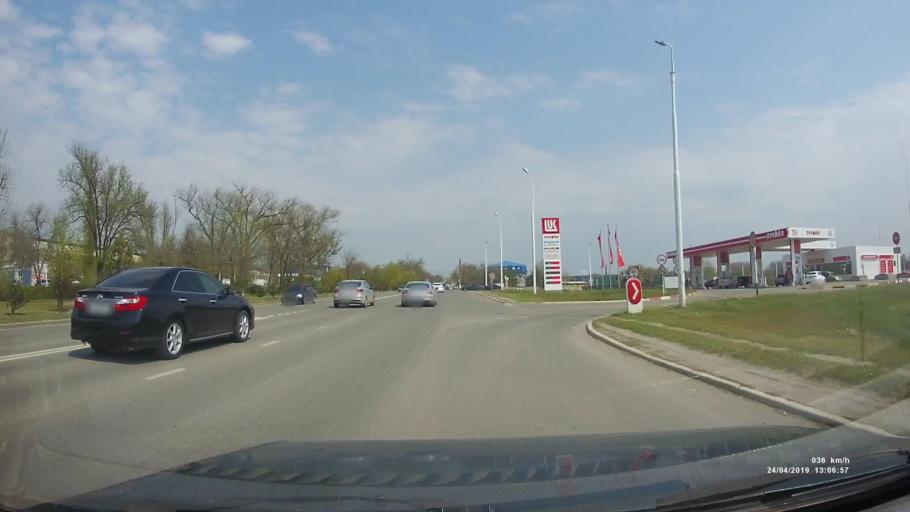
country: RU
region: Kalmykiya
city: Elista
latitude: 46.3119
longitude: 44.2928
